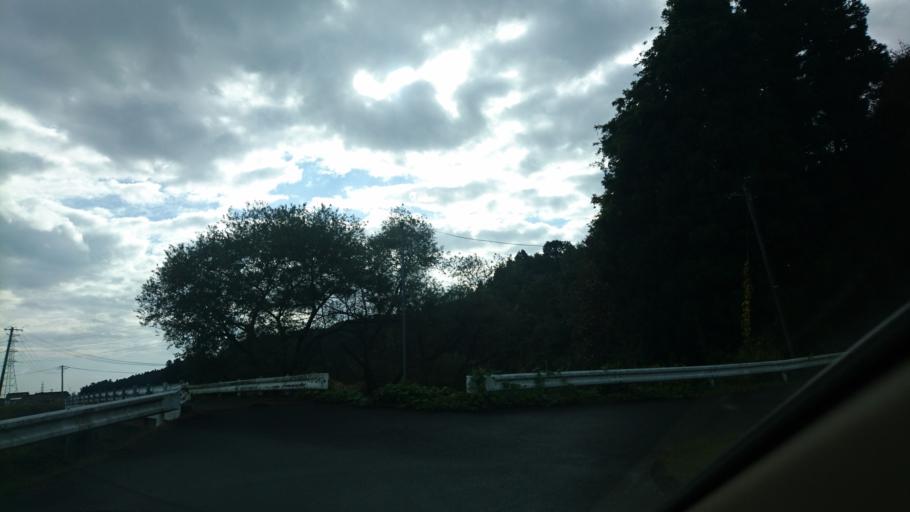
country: JP
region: Iwate
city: Ichinoseki
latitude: 38.7947
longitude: 140.9909
